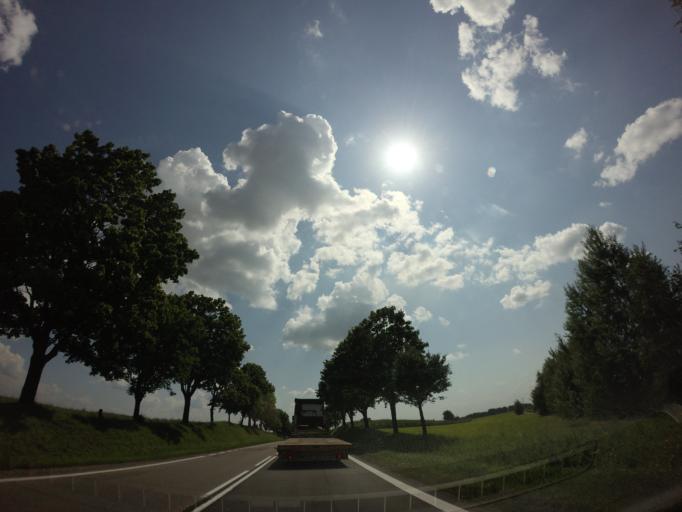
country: PL
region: Podlasie
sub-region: Powiat lomzynski
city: Piatnica
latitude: 53.2223
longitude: 22.1087
